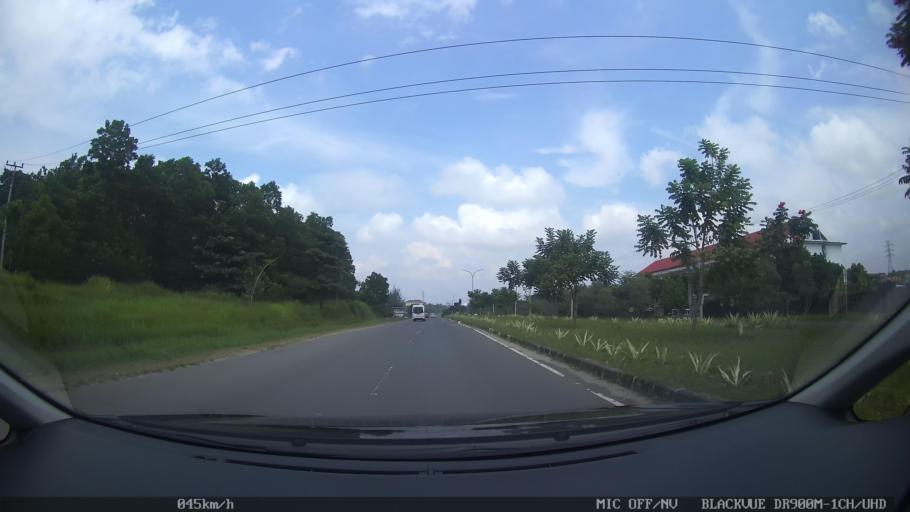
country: ID
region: Lampung
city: Kedaton
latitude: -5.3562
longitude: 105.3165
